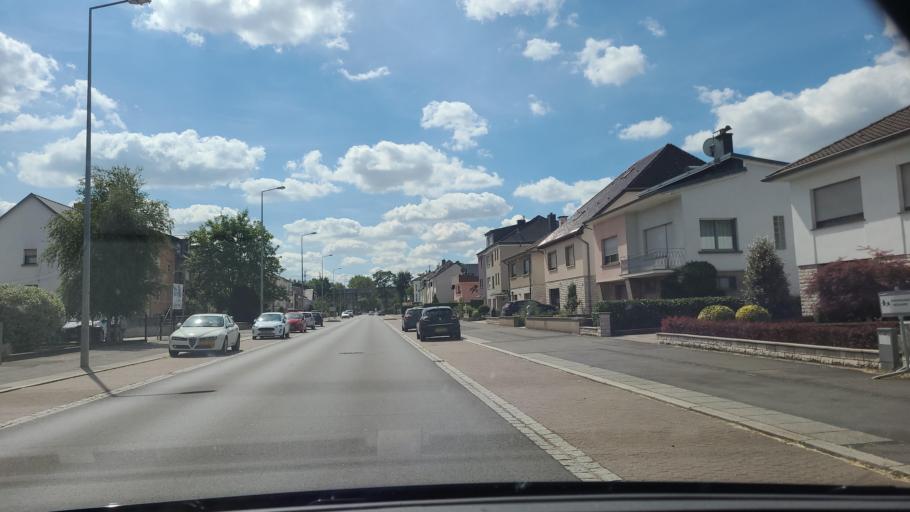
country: LU
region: Luxembourg
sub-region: Canton d'Esch-sur-Alzette
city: Petange
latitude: 49.5582
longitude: 5.8965
